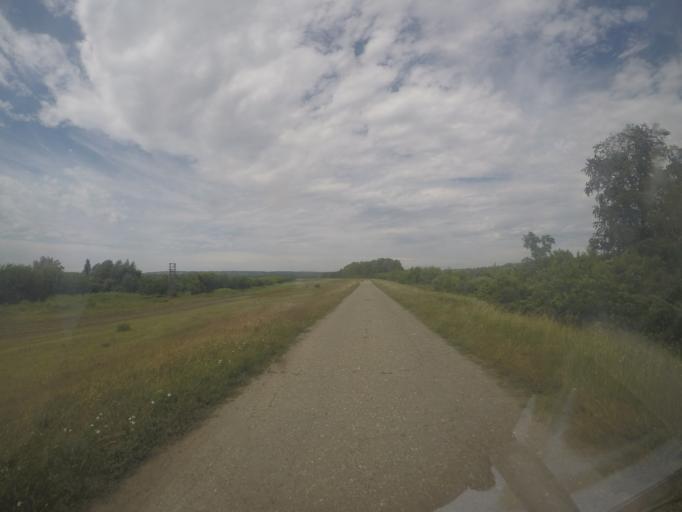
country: RS
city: Knicanin
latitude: 45.1780
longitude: 20.3024
